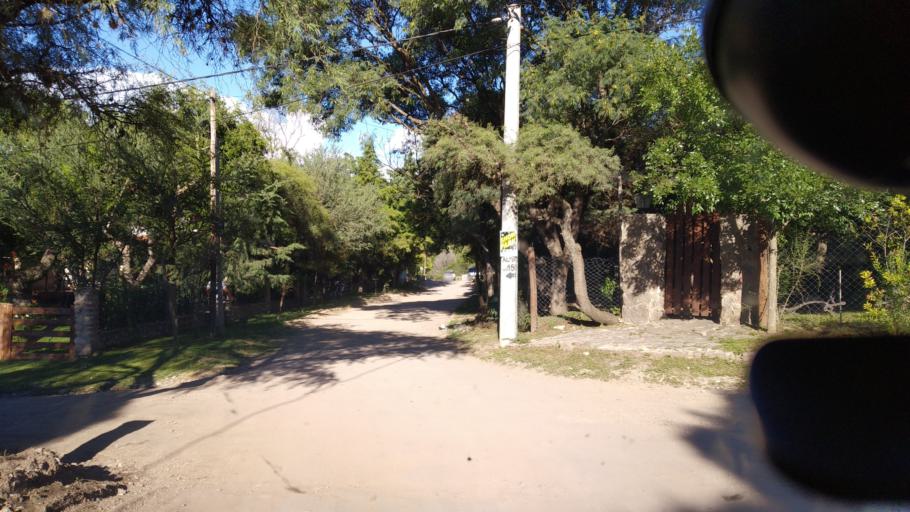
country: AR
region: Cordoba
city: Mina Clavero
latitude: -31.7273
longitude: -64.9960
